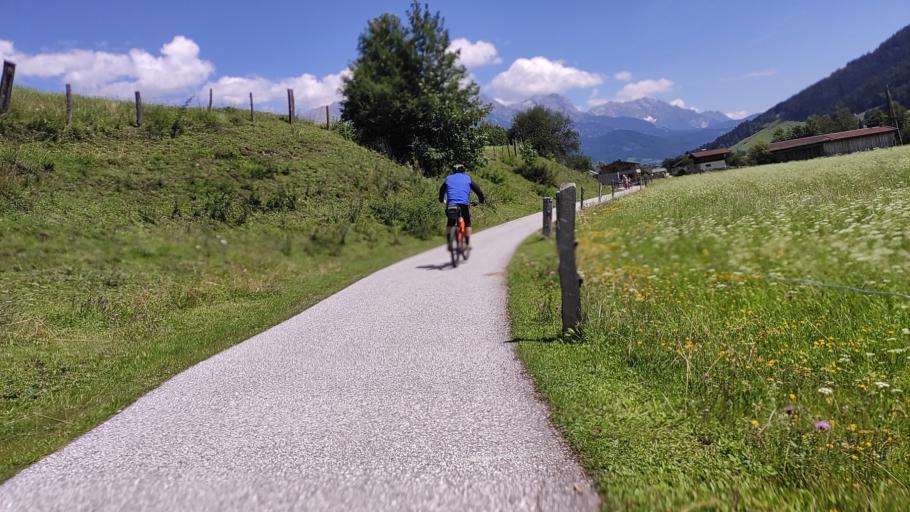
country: AT
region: Salzburg
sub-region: Politischer Bezirk Zell am See
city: Leogang
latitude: 47.4415
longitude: 12.7738
